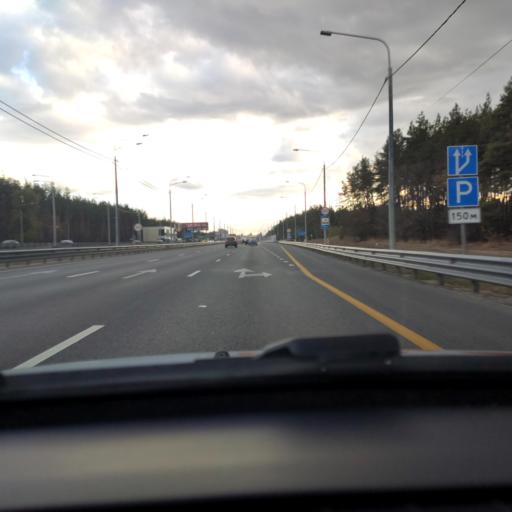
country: RU
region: Voronezj
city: Podgornoye
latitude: 51.7473
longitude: 39.1841
